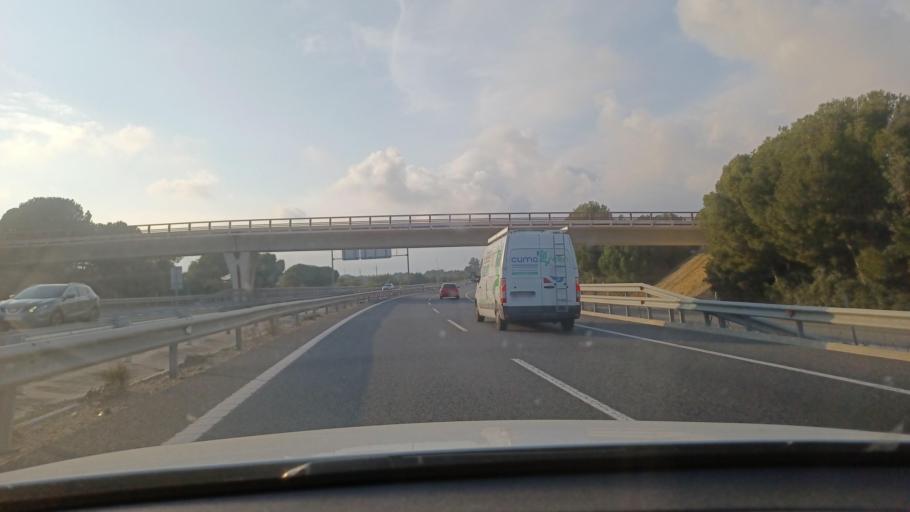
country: ES
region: Catalonia
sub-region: Provincia de Tarragona
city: Vila-seca
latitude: 41.1014
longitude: 1.1439
